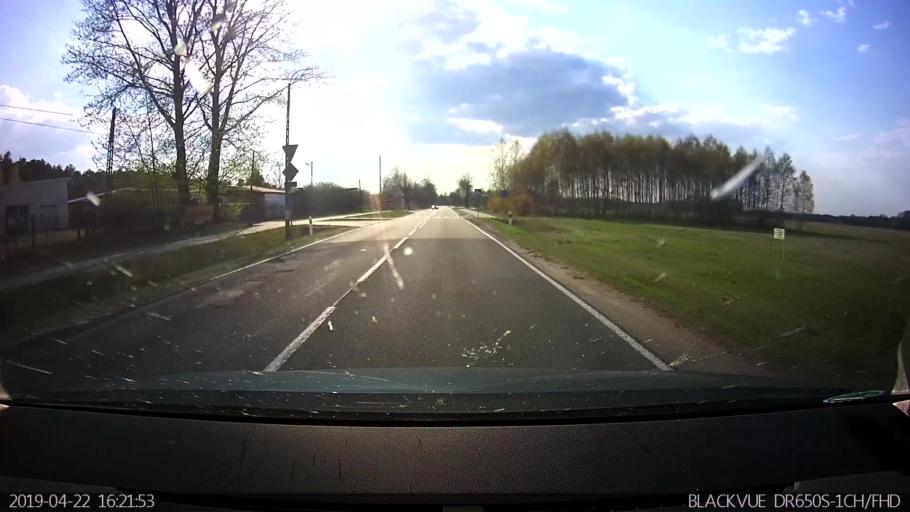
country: PL
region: Podlasie
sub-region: Powiat hajnowski
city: Kleszczele
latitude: 52.5634
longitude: 23.3161
